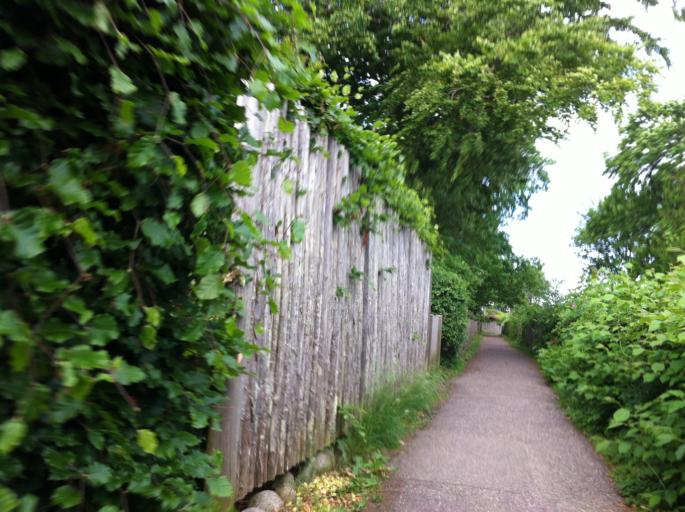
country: DK
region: Capital Region
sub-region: Gribskov Kommune
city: Gilleleje
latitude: 56.1275
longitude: 12.2920
